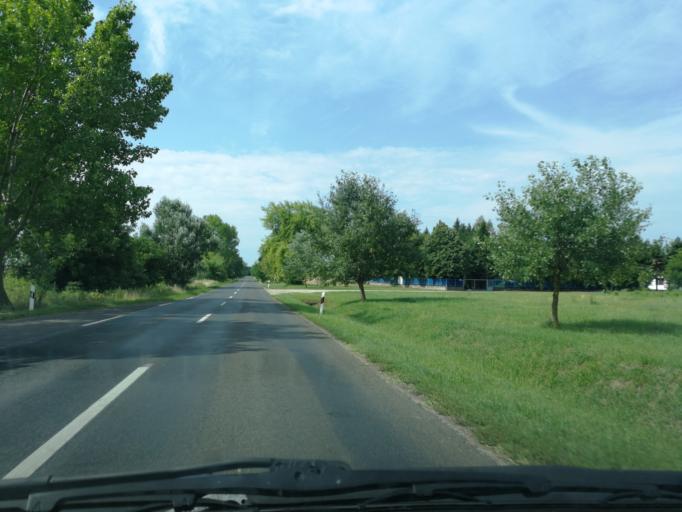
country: HU
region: Bacs-Kiskun
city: Davod
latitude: 46.0156
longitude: 18.9396
